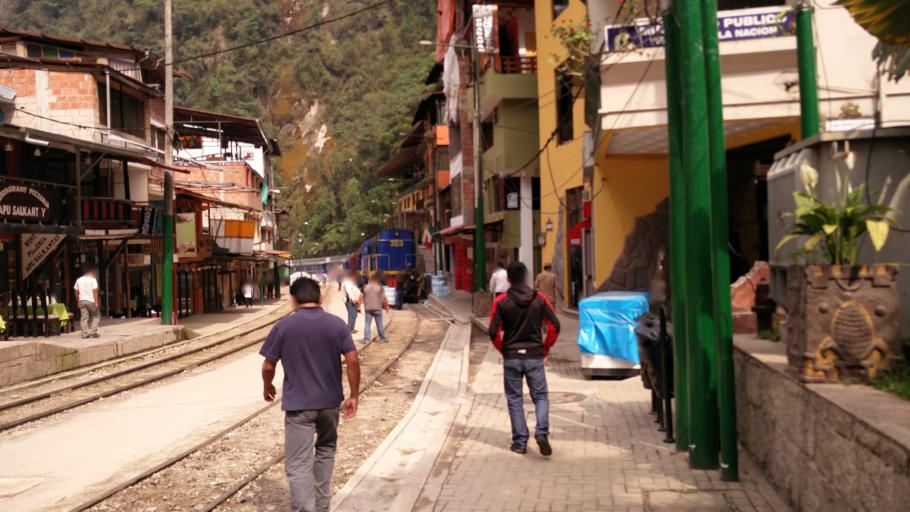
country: PE
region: Cusco
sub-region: Provincia de La Convencion
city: Santa Teresa
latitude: -13.1544
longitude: -72.5262
